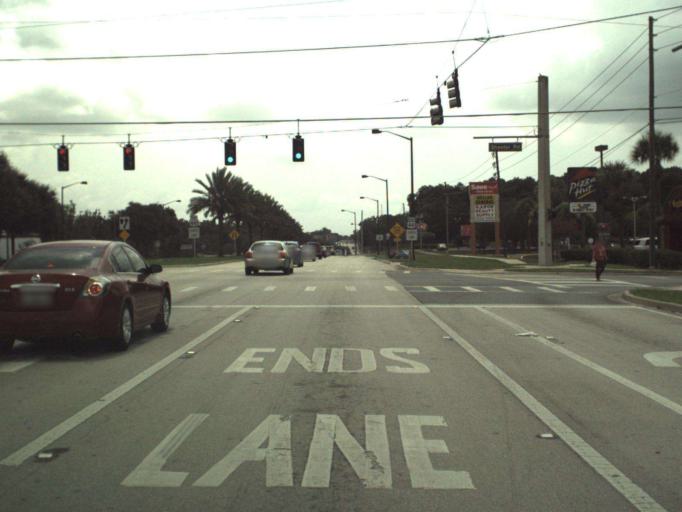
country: US
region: Florida
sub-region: Orange County
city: Apopka
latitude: 28.6731
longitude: -81.4924
